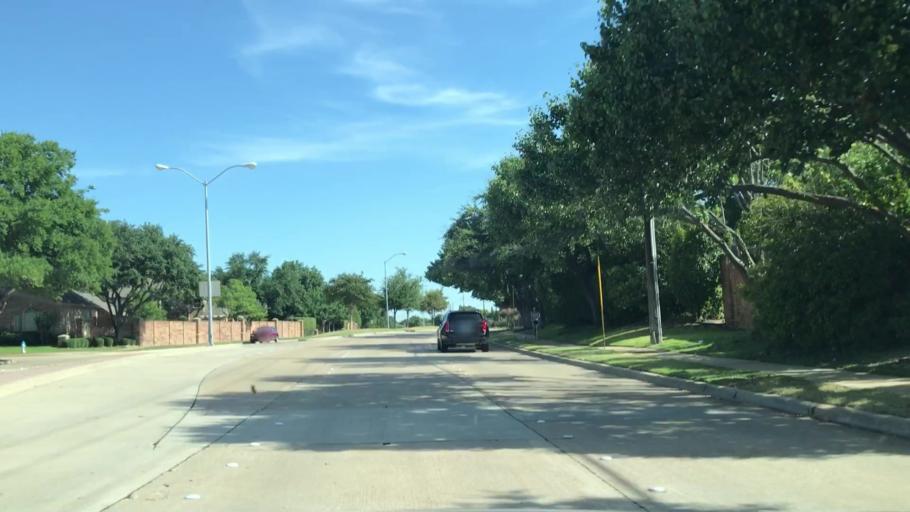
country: US
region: Texas
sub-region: Denton County
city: The Colony
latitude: 33.0476
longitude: -96.8394
